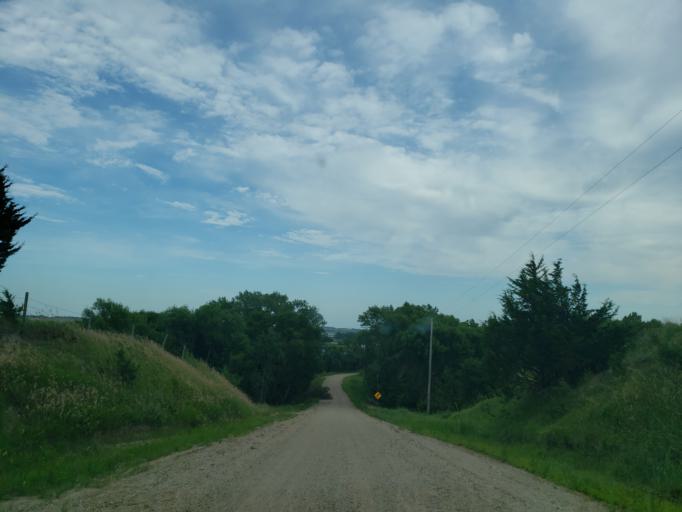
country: US
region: South Dakota
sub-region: Davison County
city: Mitchell
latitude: 43.6849
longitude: -97.9692
